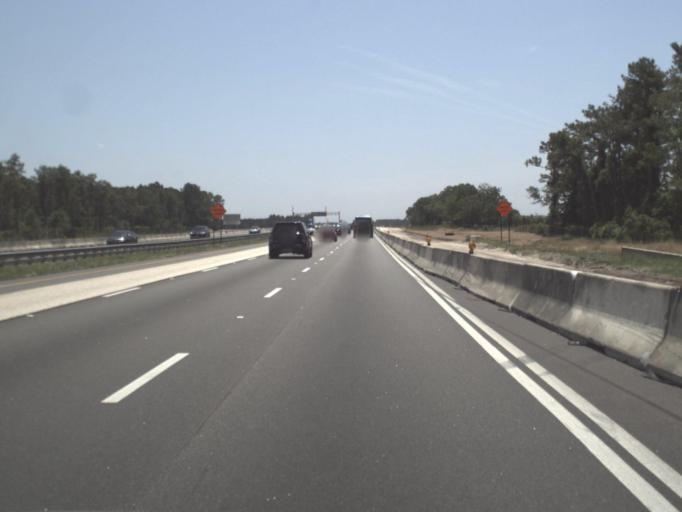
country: US
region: Florida
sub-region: Saint Johns County
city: Fruit Cove
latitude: 30.1252
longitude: -81.5248
